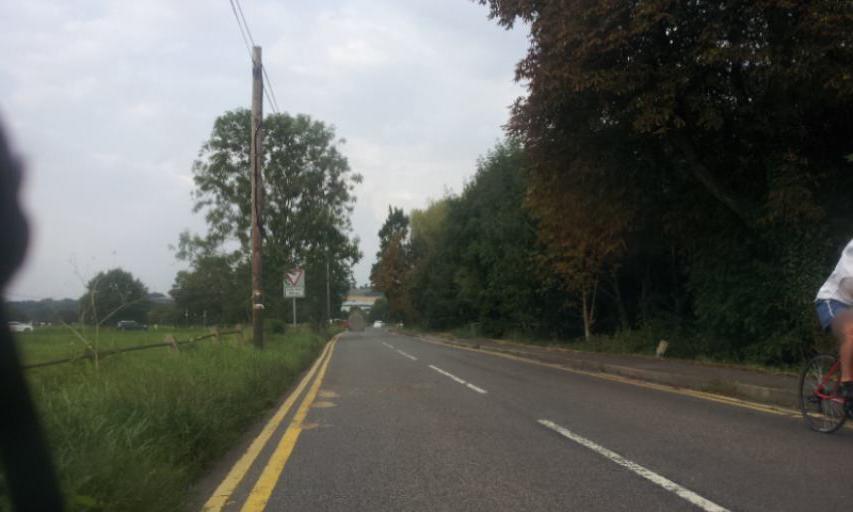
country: GB
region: England
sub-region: Kent
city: Yalding
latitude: 51.2200
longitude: 0.4213
